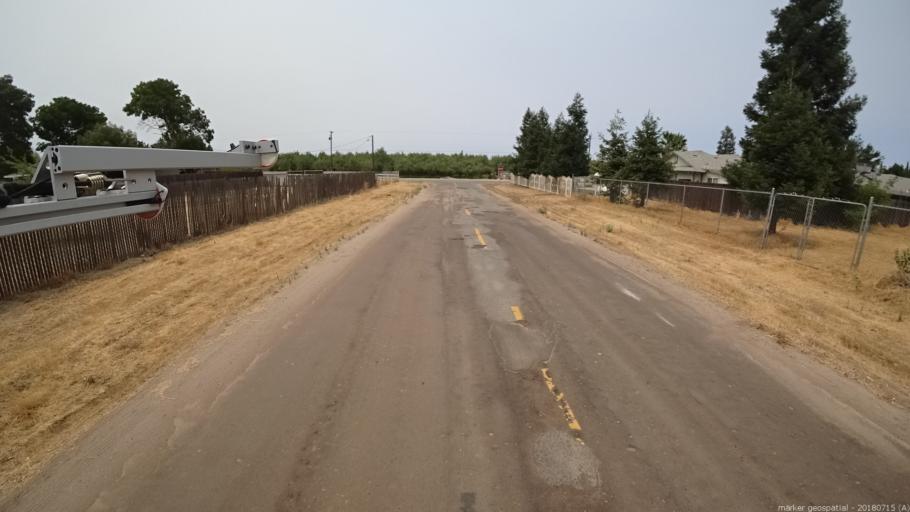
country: US
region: California
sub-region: Madera County
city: Madera Acres
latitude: 37.0104
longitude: -120.1018
